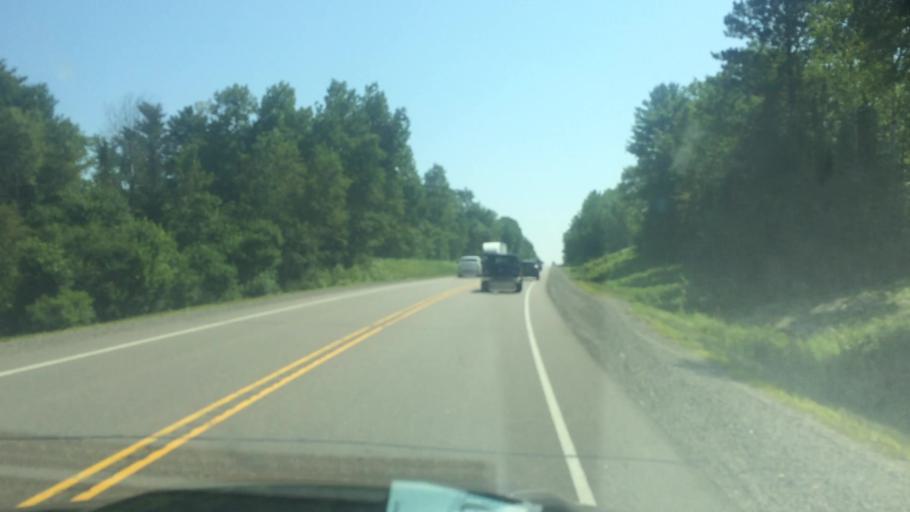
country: US
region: Wisconsin
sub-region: Lincoln County
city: Tomahawk
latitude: 45.5706
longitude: -89.6080
